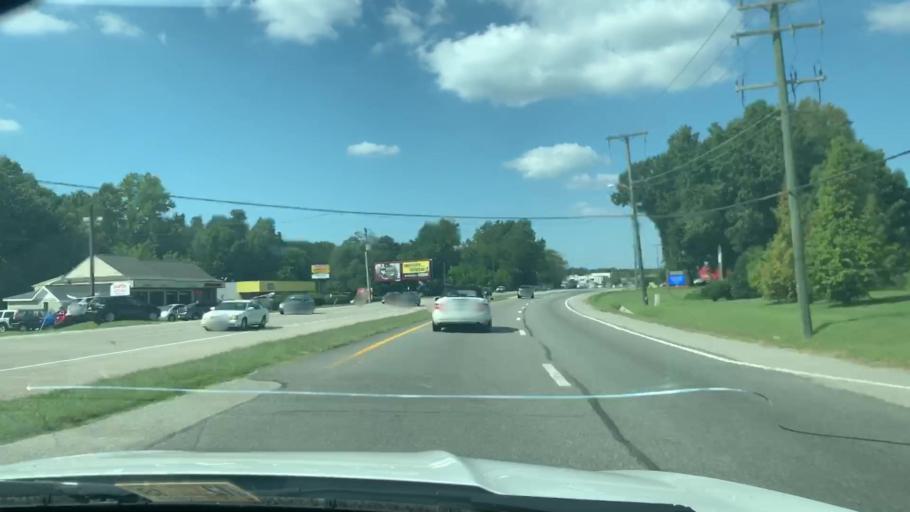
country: US
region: Virginia
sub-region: York County
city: Yorktown
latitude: 37.1679
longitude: -76.4700
